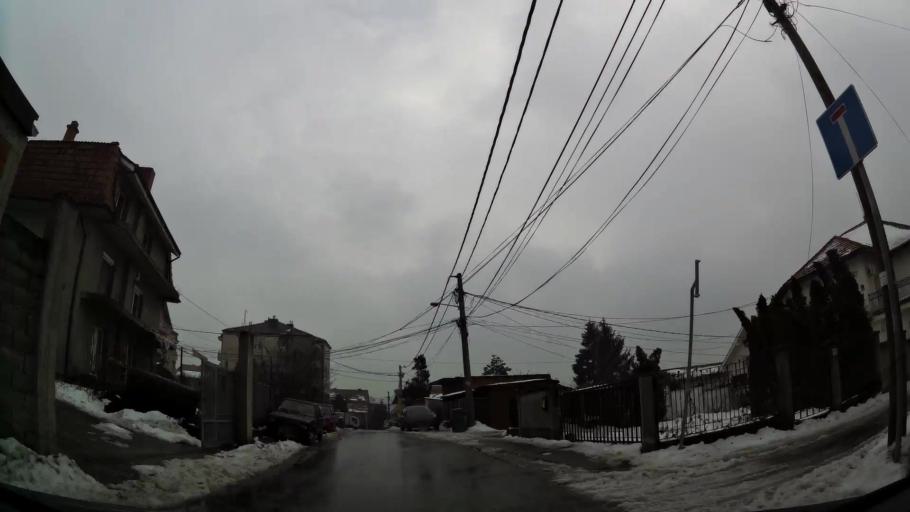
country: RS
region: Central Serbia
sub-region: Belgrade
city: Zvezdara
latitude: 44.7761
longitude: 20.5242
